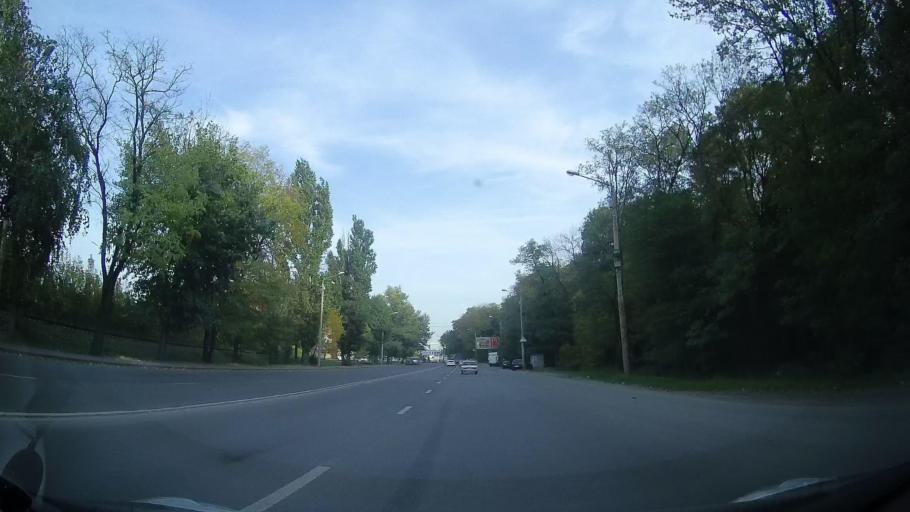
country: RU
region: Rostov
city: Aksay
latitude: 47.2749
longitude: 39.8132
